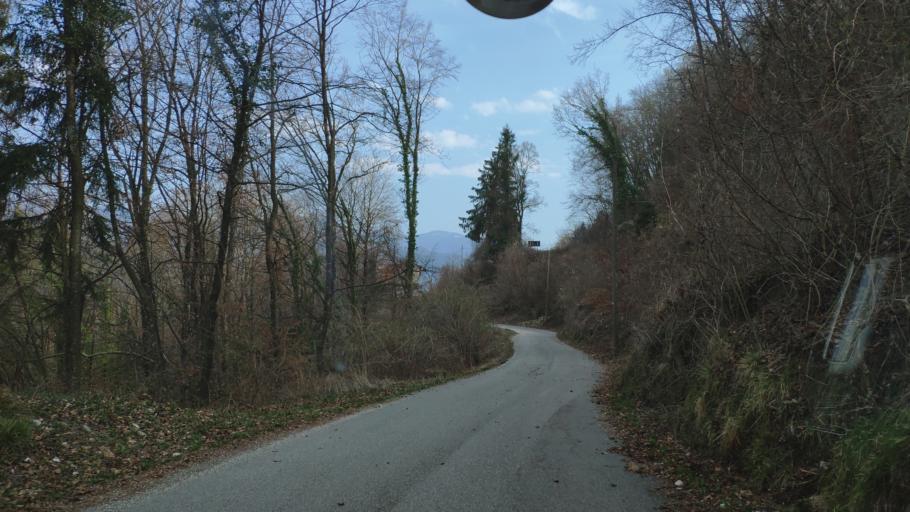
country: IT
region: Veneto
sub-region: Provincia di Vicenza
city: Enego
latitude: 45.9494
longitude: 11.7114
